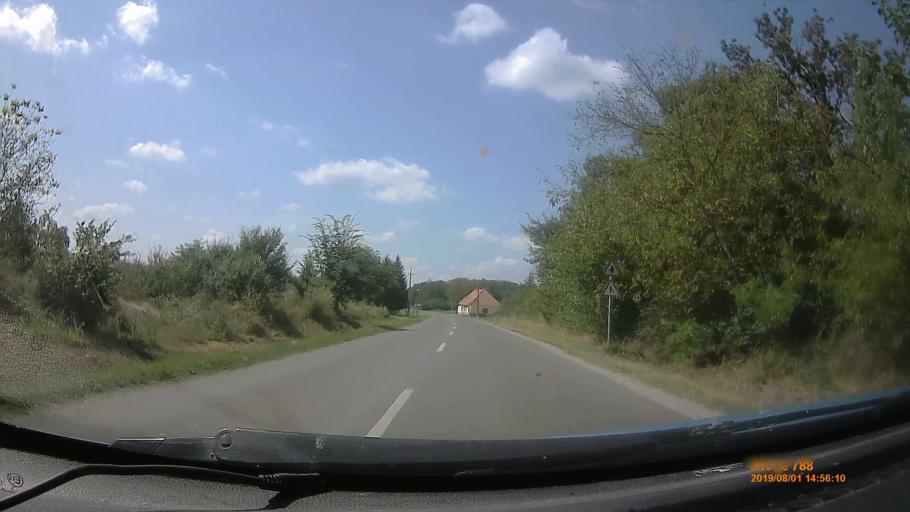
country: HU
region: Baranya
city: Vajszlo
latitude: 45.8751
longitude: 17.9476
